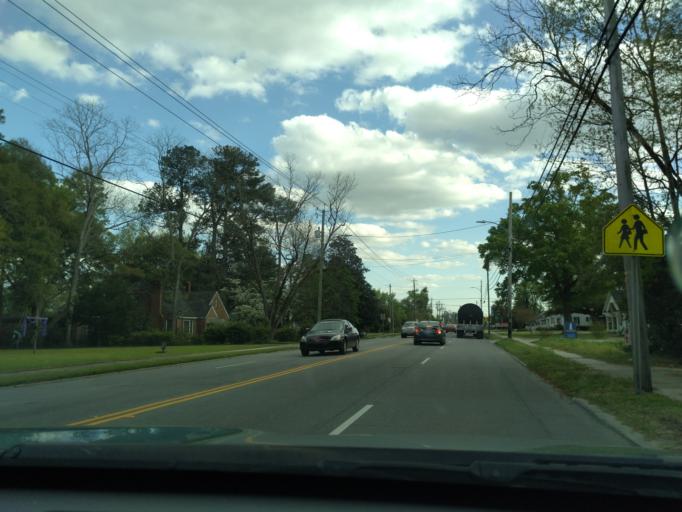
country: US
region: South Carolina
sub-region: Williamsburg County
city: Kingstree
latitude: 33.6699
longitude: -79.8357
